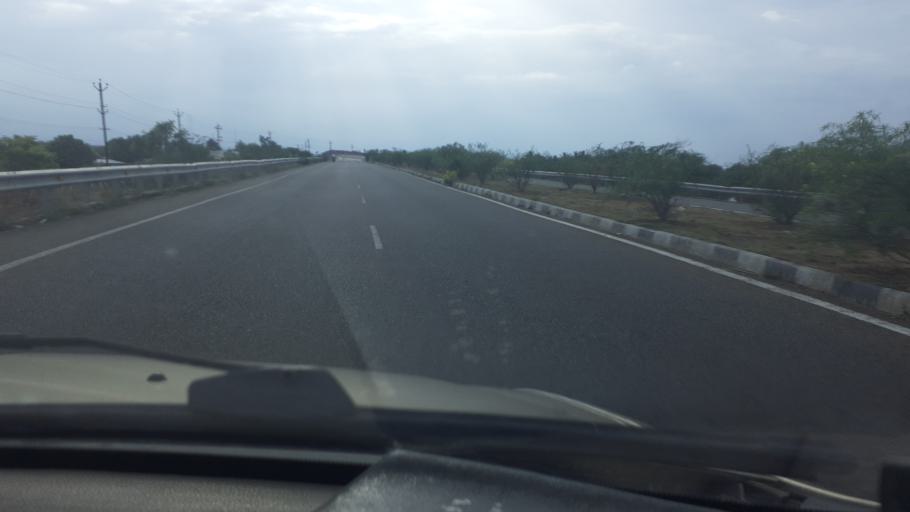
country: IN
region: Tamil Nadu
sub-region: Tirunelveli Kattabo
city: Tirunelveli
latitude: 8.6671
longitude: 77.7433
